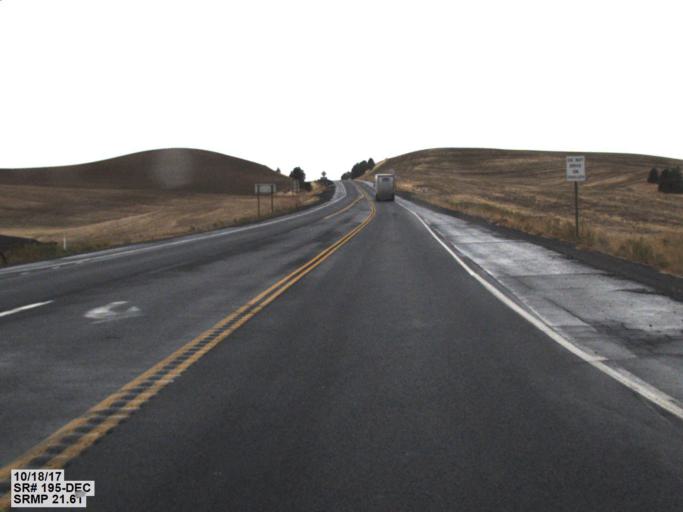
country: US
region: Washington
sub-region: Whitman County
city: Pullman
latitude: 46.7254
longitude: -117.2225
